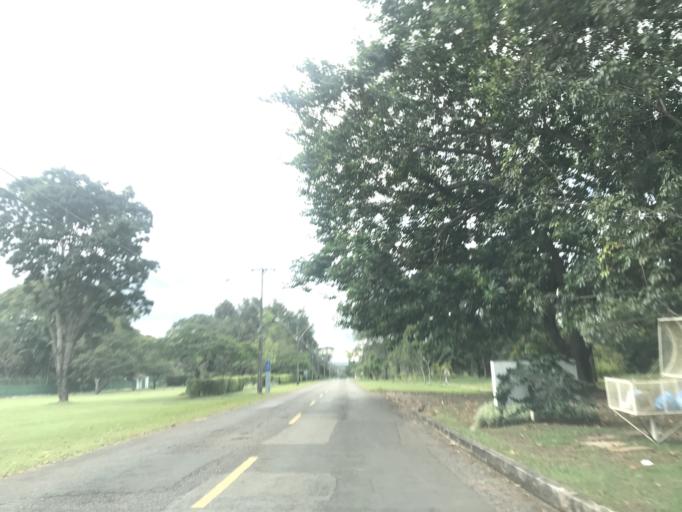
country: BR
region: Federal District
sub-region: Brasilia
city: Brasilia
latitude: -15.9051
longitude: -47.9399
